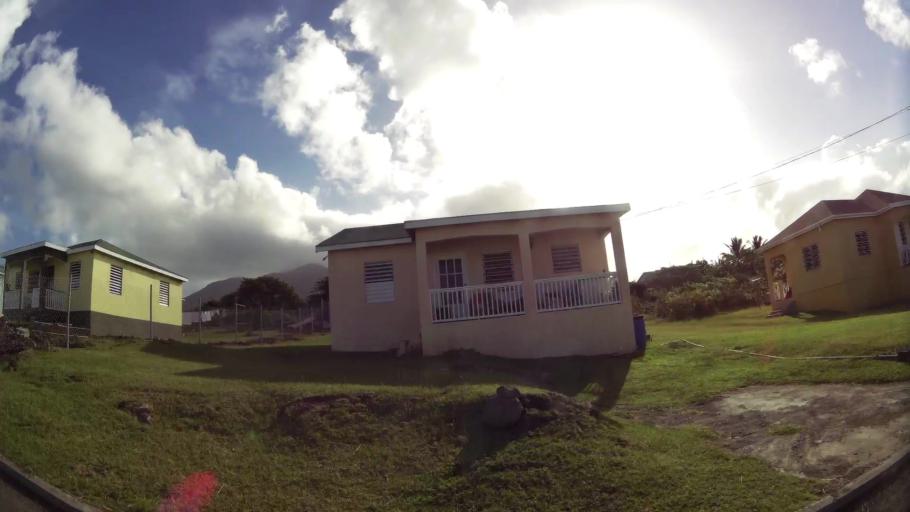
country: KN
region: Saint Paul Charlestown
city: Charlestown
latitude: 17.1420
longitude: -62.6207
